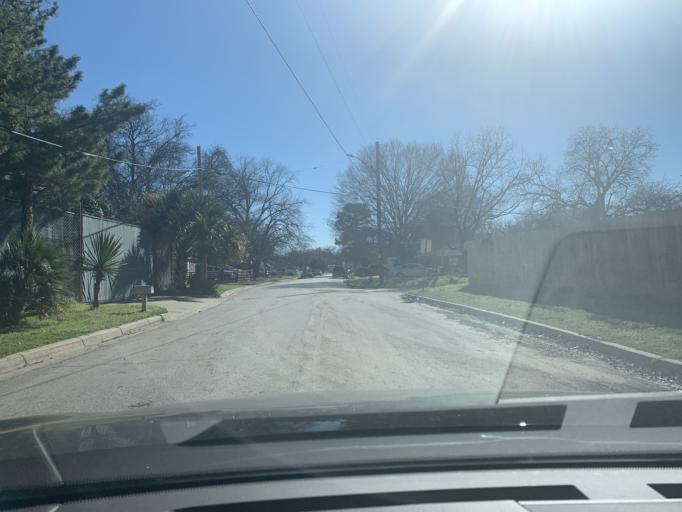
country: US
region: Texas
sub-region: Tarrant County
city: Haltom City
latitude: 32.7674
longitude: -97.2903
